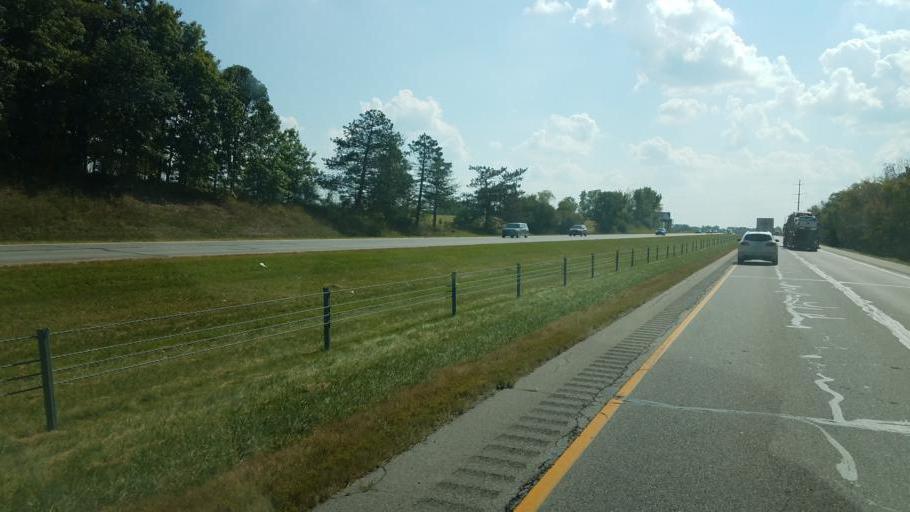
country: US
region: Indiana
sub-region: DeKalb County
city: Garrett
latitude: 41.2723
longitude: -85.0870
